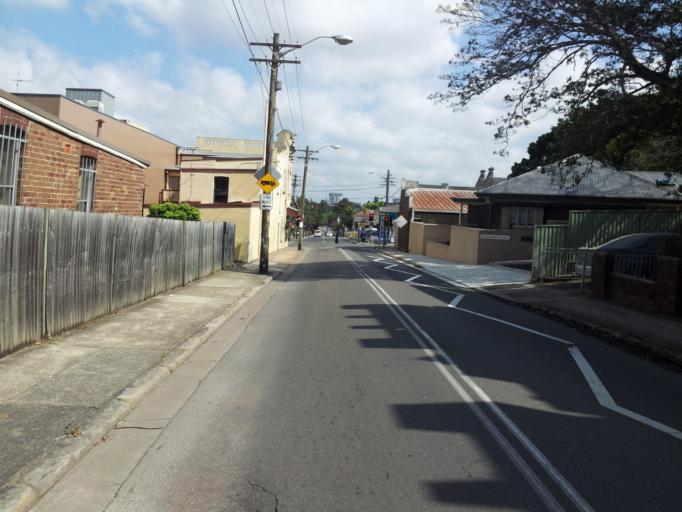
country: AU
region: New South Wales
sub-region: Ashfield
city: Ashfield
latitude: -33.8871
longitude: 151.1266
